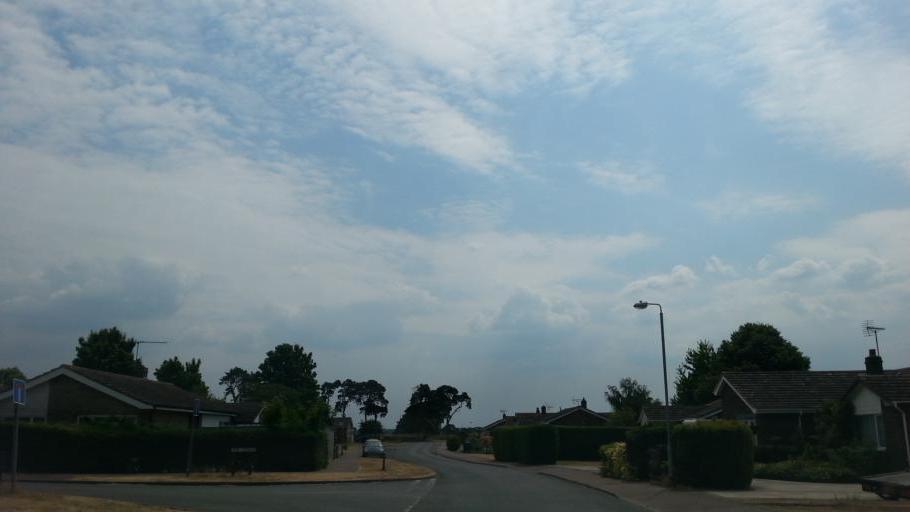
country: GB
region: England
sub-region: Suffolk
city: Lakenheath
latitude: 52.4136
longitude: 0.5298
